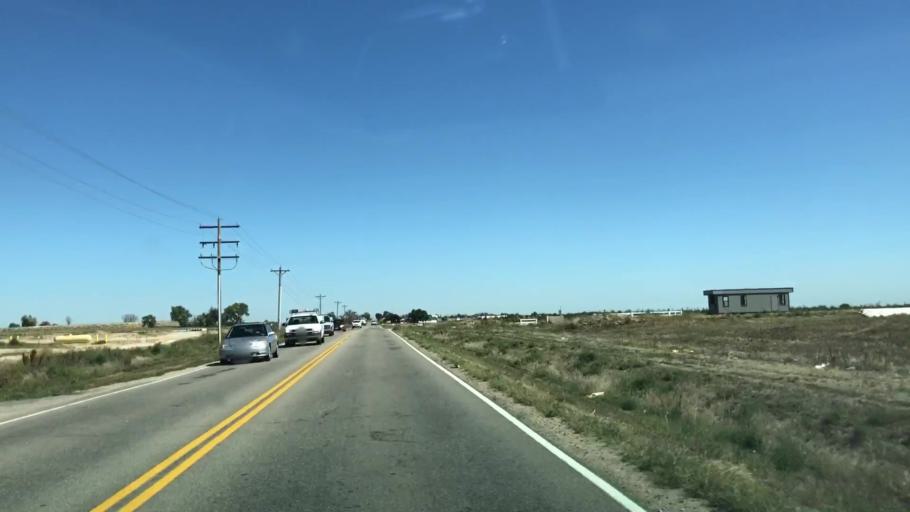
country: US
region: Colorado
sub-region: Weld County
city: Windsor
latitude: 40.5228
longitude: -104.9406
